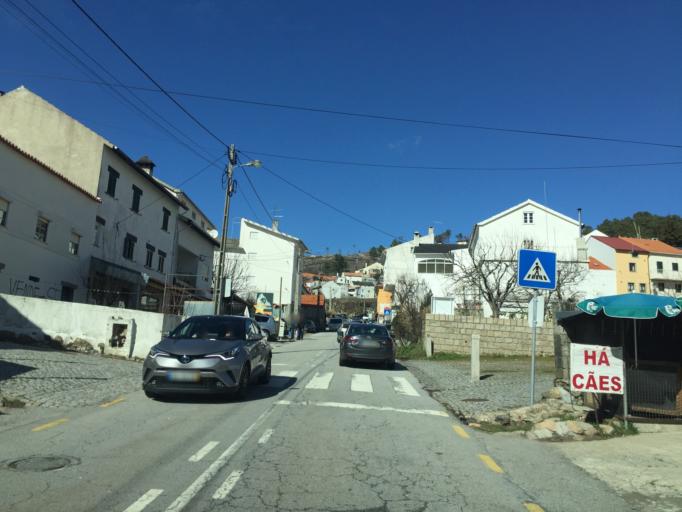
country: PT
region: Guarda
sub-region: Seia
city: Seia
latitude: 40.4015
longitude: -7.6411
